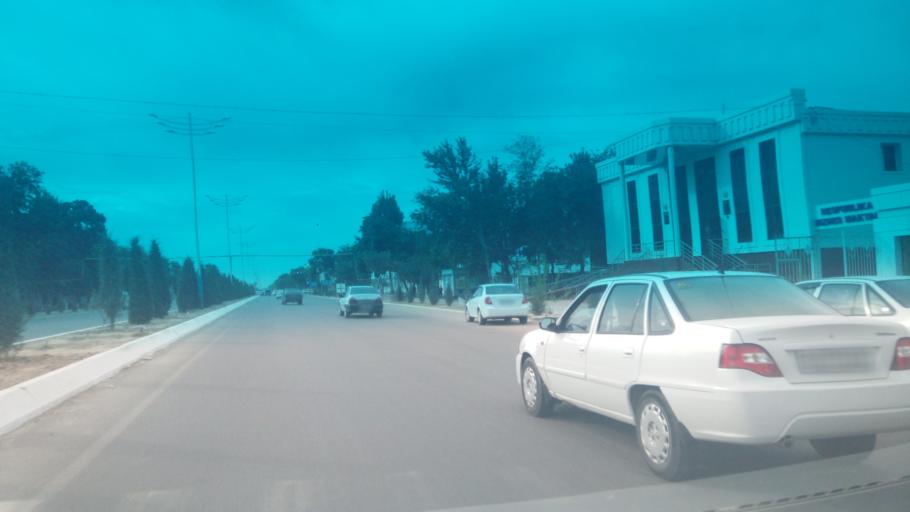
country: UZ
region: Sirdaryo
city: Guliston
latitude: 40.5121
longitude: 68.7702
